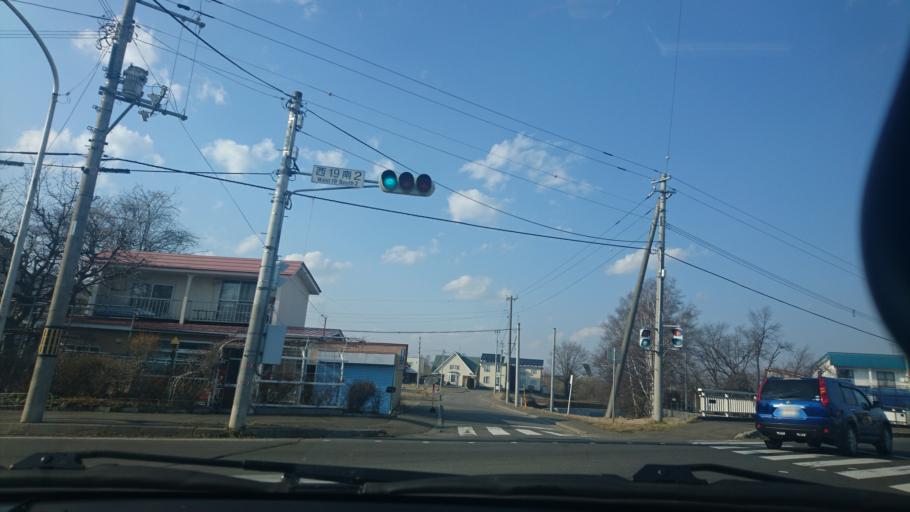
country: JP
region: Hokkaido
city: Obihiro
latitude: 42.9226
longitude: 143.1574
